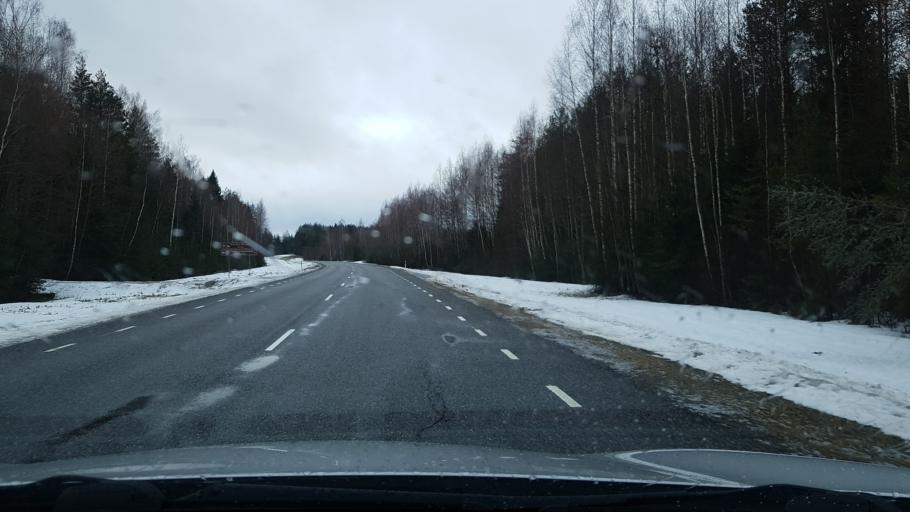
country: LV
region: Apes Novads
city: Ape
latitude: 57.6377
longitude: 26.6412
